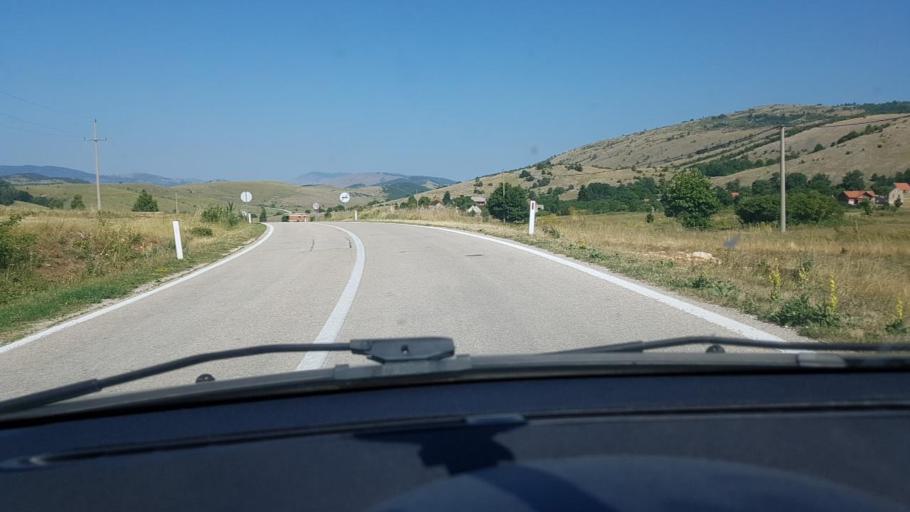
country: BA
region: Federation of Bosnia and Herzegovina
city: Bosansko Grahovo
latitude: 44.1229
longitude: 16.5299
